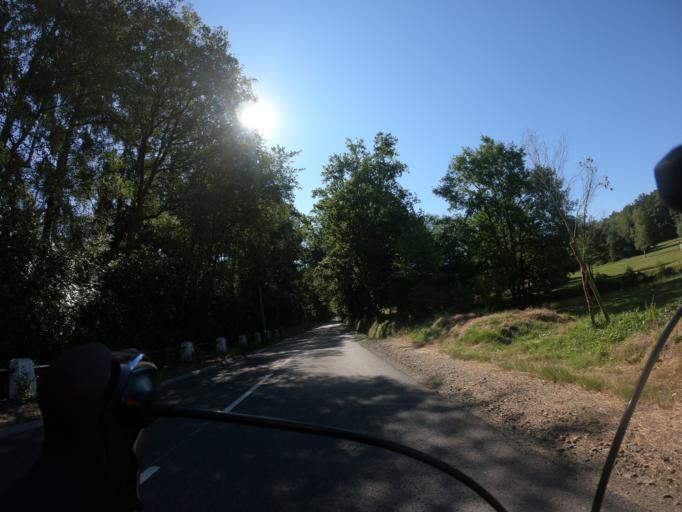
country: FR
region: Lower Normandy
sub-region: Departement de l'Orne
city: Tesse-la-Madeleine
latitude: 48.5642
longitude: -0.4334
